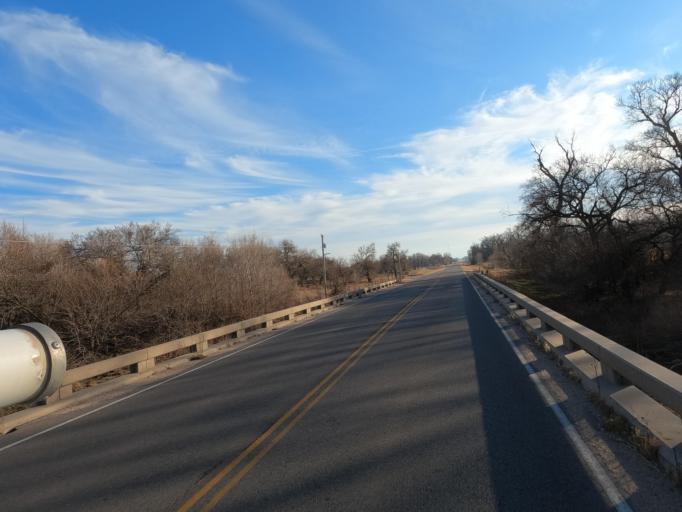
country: US
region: Kansas
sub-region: Reno County
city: Buhler
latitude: 38.1204
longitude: -97.7757
